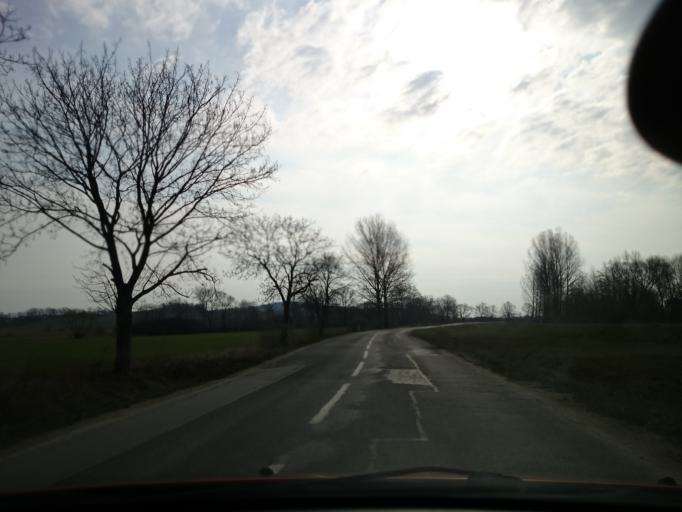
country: PL
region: Lower Silesian Voivodeship
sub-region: Powiat zabkowicki
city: Kamieniec Zabkowicki
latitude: 50.5113
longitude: 16.9280
